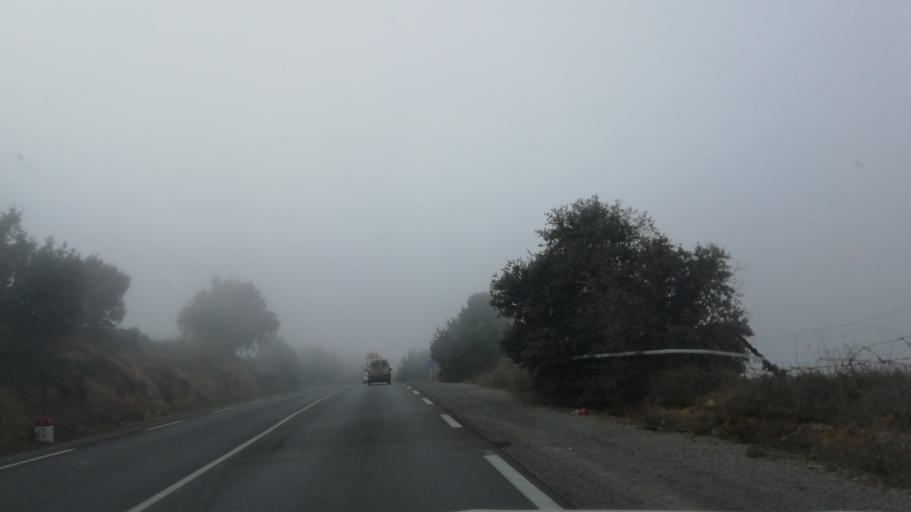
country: DZ
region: Mascara
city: Mascara
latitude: 35.5241
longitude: 0.3239
